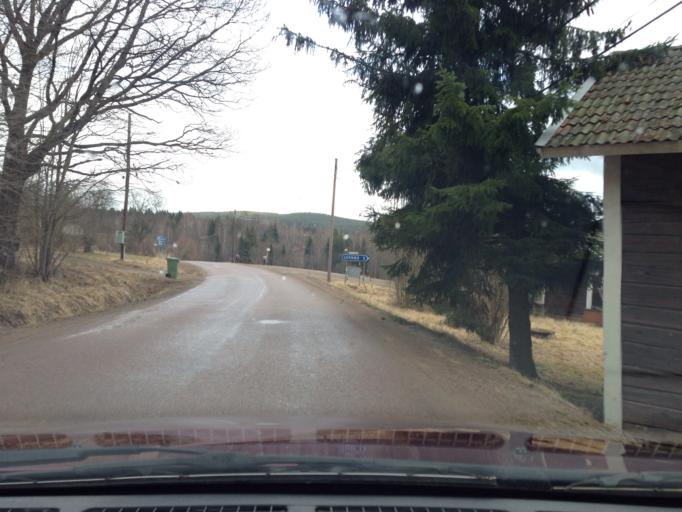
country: SE
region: Dalarna
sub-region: Smedjebackens Kommun
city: Smedjebacken
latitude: 60.1776
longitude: 15.3047
